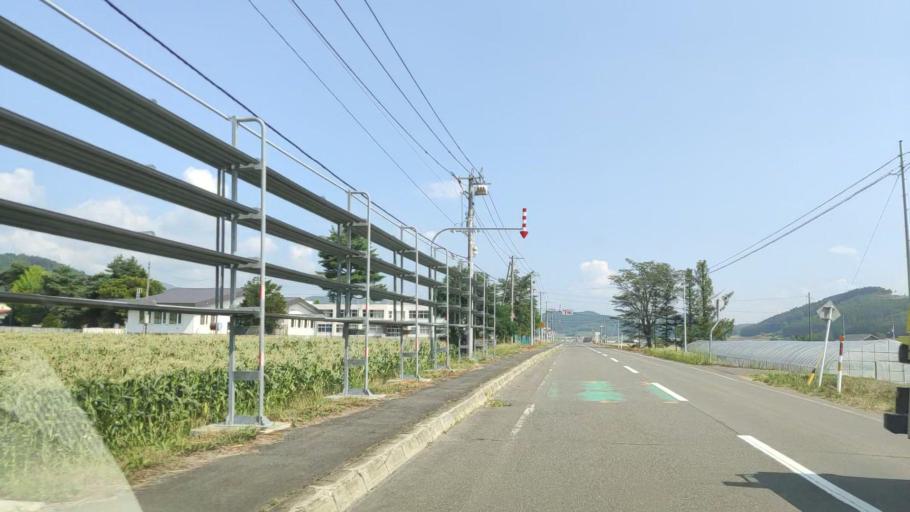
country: JP
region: Hokkaido
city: Shimo-furano
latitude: 43.3912
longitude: 142.3948
